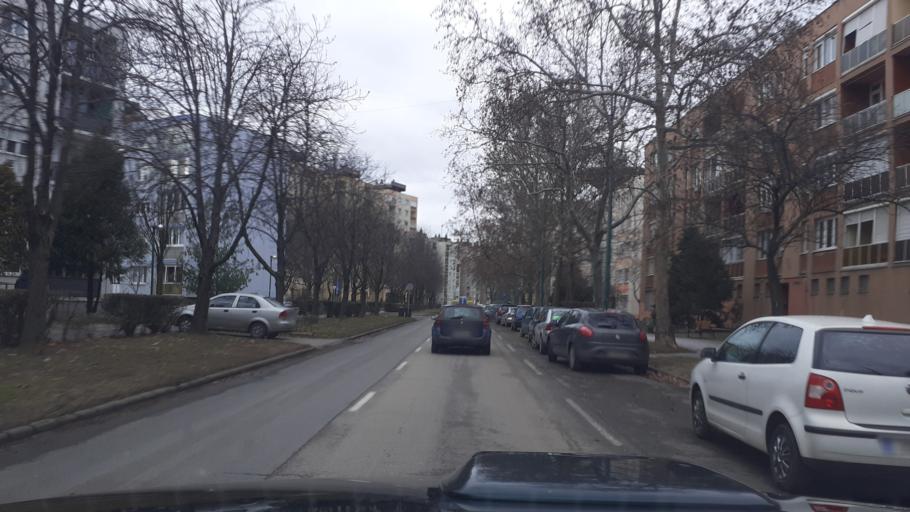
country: HU
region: Fejer
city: dunaujvaros
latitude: 46.9717
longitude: 18.9366
